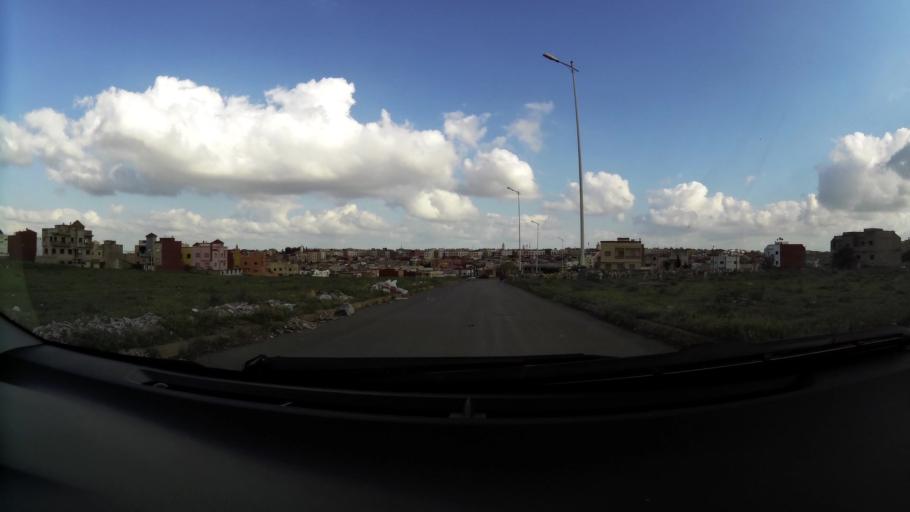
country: MA
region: Chaouia-Ouardigha
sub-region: Settat Province
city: Settat
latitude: 33.0090
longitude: -7.6405
